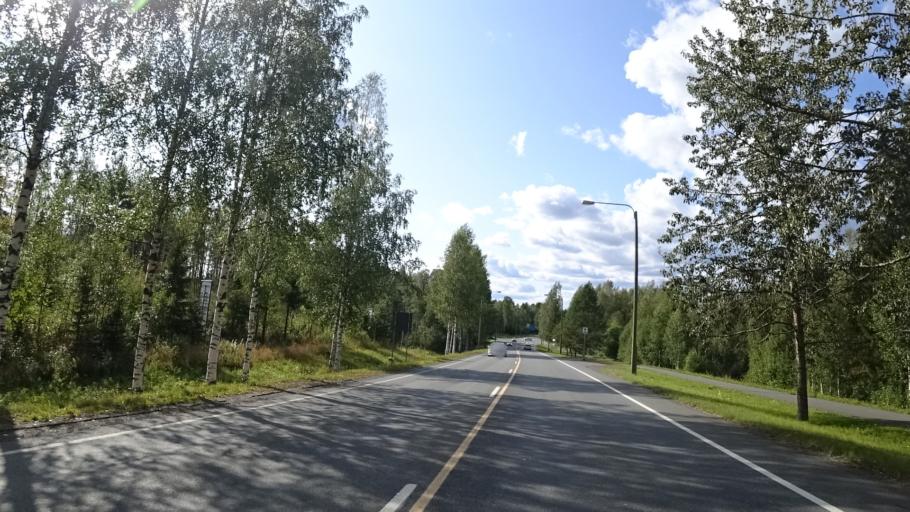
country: FI
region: North Karelia
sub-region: Keski-Karjala
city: Tohmajaervi
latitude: 62.2285
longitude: 30.3254
